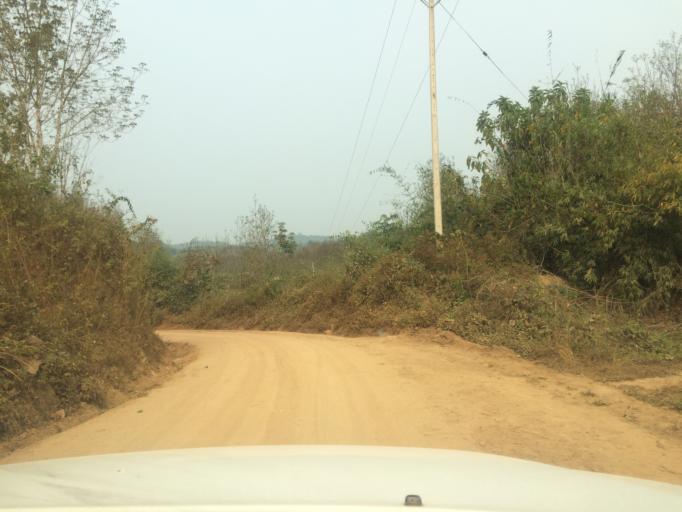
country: LA
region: Loungnamtha
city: Muang Nale
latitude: 20.4162
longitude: 101.6779
